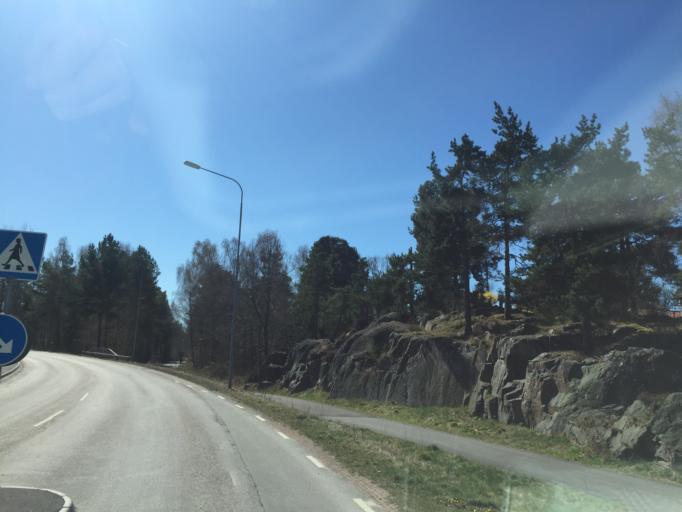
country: SE
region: Kalmar
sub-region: Oskarshamns Kommun
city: Oskarshamn
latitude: 57.2489
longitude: 16.4605
